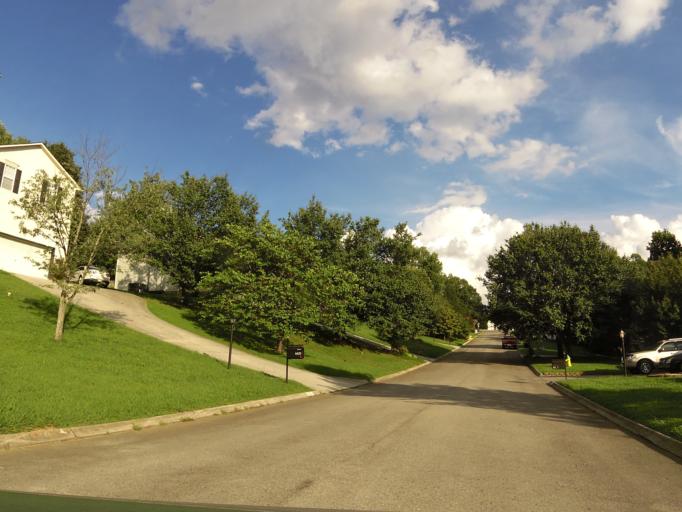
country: US
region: Tennessee
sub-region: Knox County
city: Knoxville
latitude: 36.0008
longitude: -84.0207
